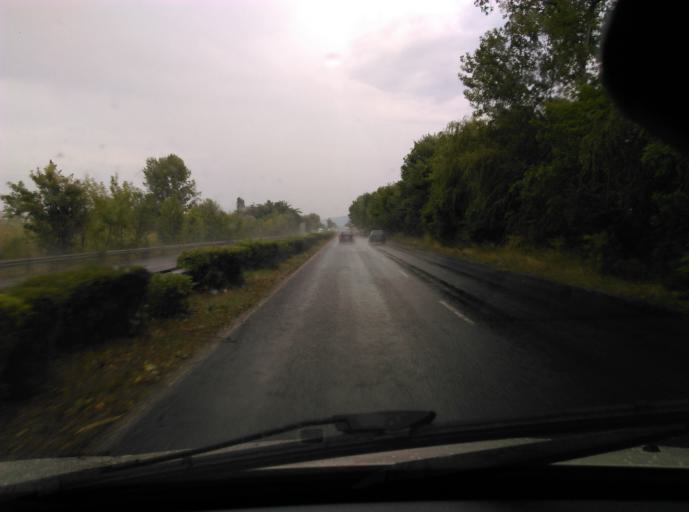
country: BG
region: Burgas
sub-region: Obshtina Burgas
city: Burgas
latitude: 42.4540
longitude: 27.4439
